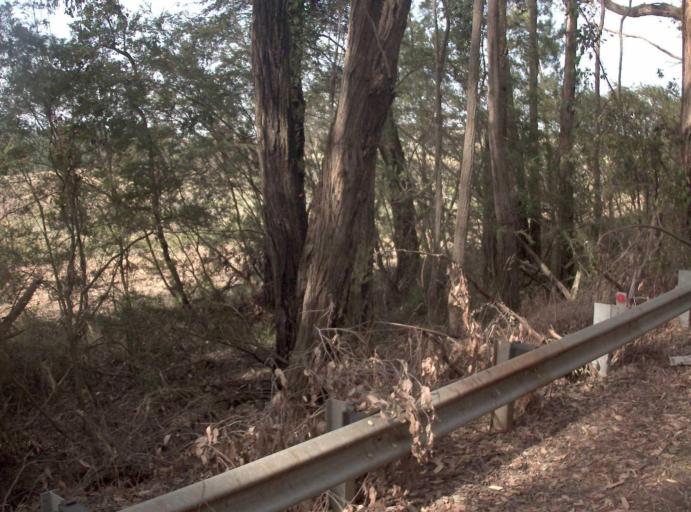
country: AU
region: Victoria
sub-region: Latrobe
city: Moe
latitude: -38.2845
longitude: 146.2573
